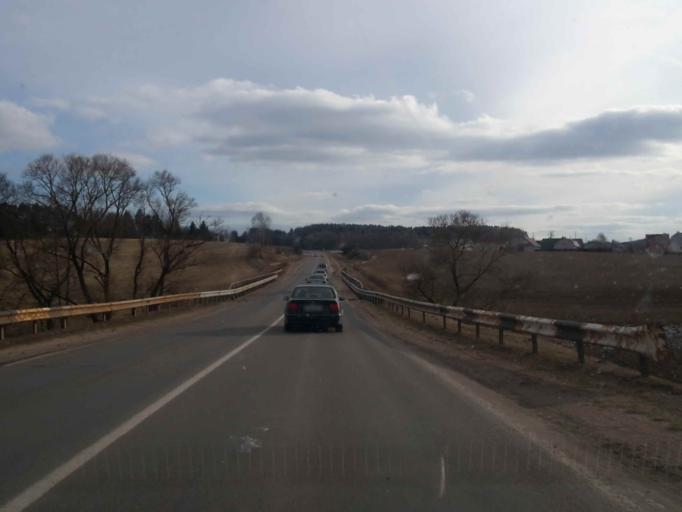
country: BY
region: Minsk
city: Bal'shavik
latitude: 54.0368
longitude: 27.5611
